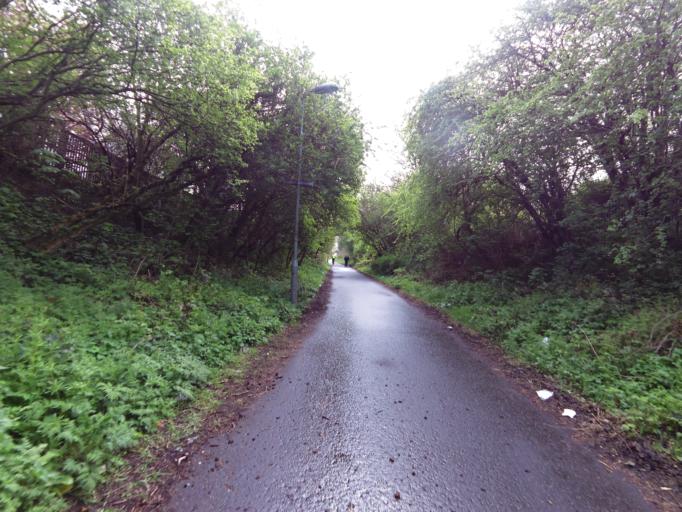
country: GB
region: Scotland
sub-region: Edinburgh
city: Colinton
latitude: 55.9659
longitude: -3.2652
